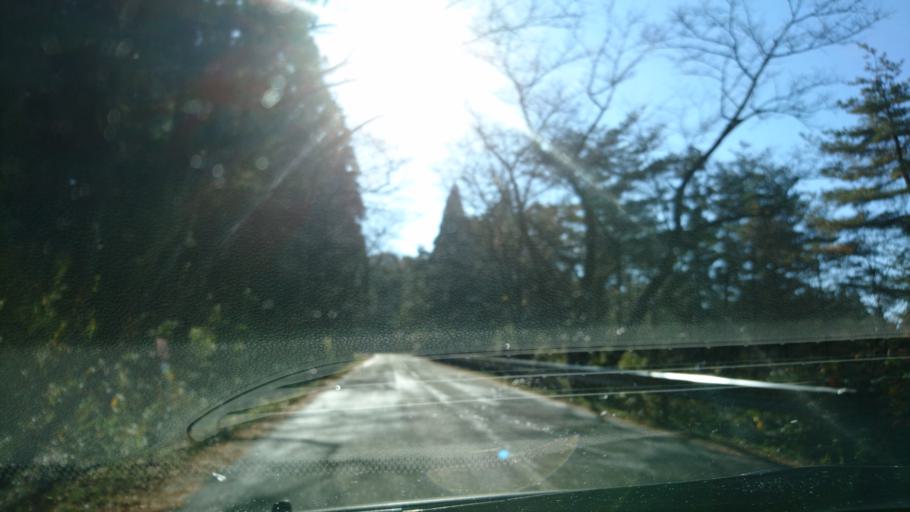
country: JP
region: Iwate
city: Ichinoseki
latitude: 38.9940
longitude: 141.0956
